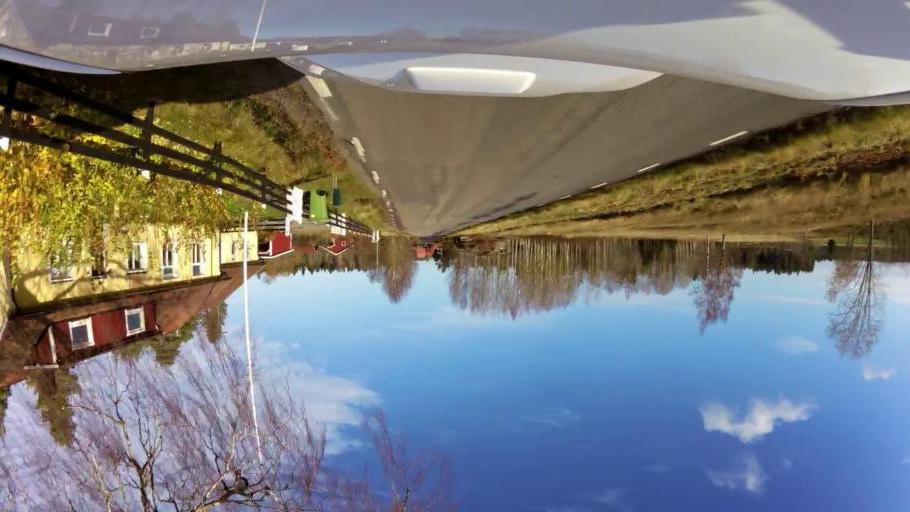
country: SE
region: OEstergoetland
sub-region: Linkopings Kommun
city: Sturefors
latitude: 58.3241
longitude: 15.6463
